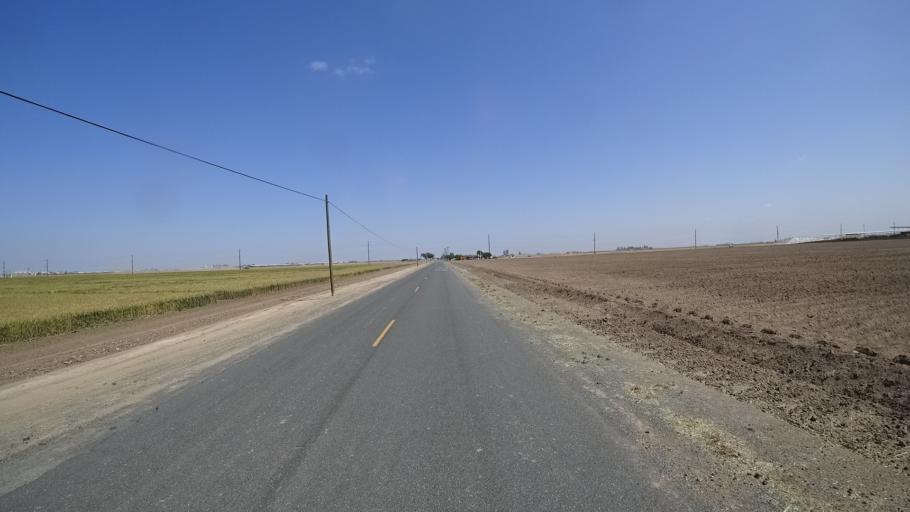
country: US
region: California
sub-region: Kings County
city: Home Garden
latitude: 36.2523
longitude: -119.6190
